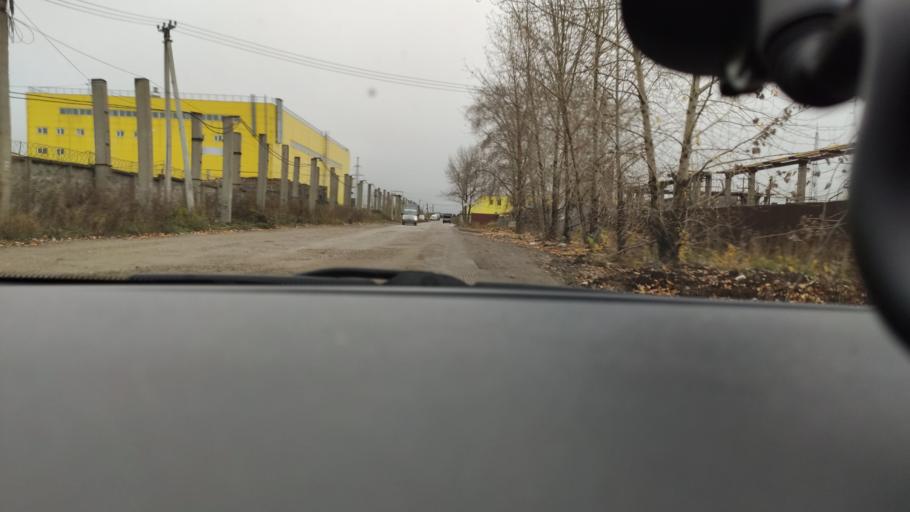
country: RU
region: Perm
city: Gamovo
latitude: 57.9134
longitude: 56.1774
